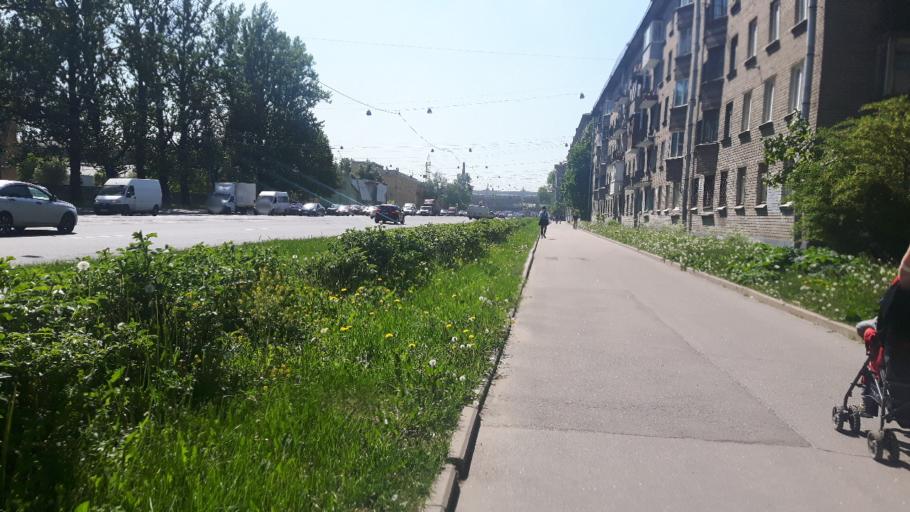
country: RU
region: St.-Petersburg
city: Avtovo
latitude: 59.8877
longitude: 30.2757
